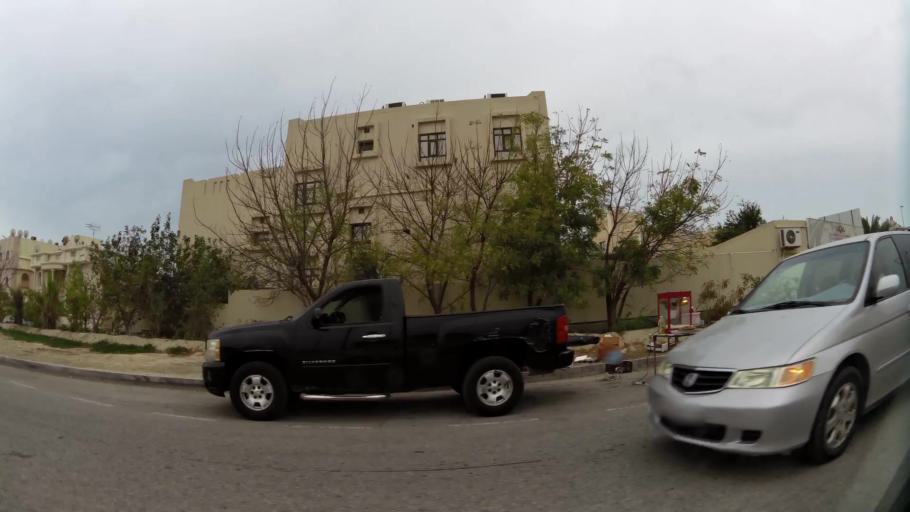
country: BH
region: Central Governorate
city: Madinat Hamad
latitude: 26.1139
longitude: 50.4994
